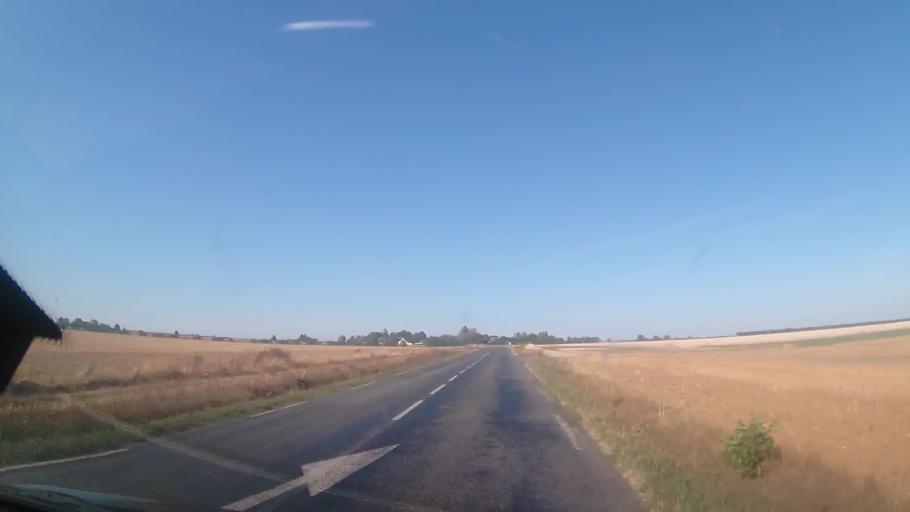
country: FR
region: Ile-de-France
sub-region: Departement de l'Essonne
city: Corbreuse
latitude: 48.4618
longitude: 1.9307
